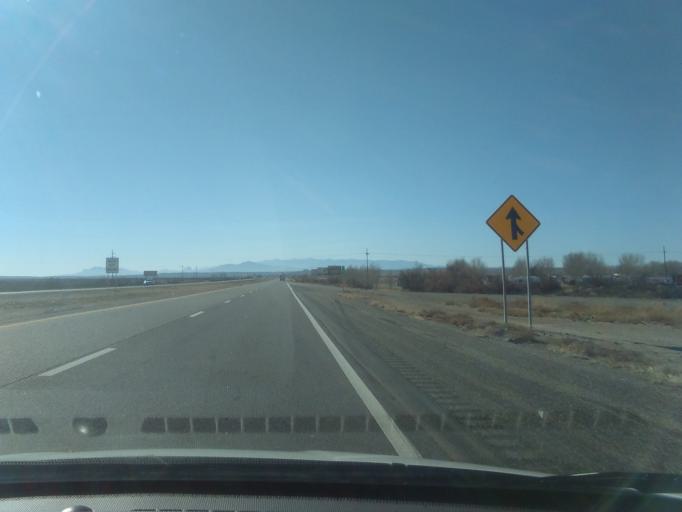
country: US
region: New Mexico
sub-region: Valencia County
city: Jarales
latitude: 34.4174
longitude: -106.8398
